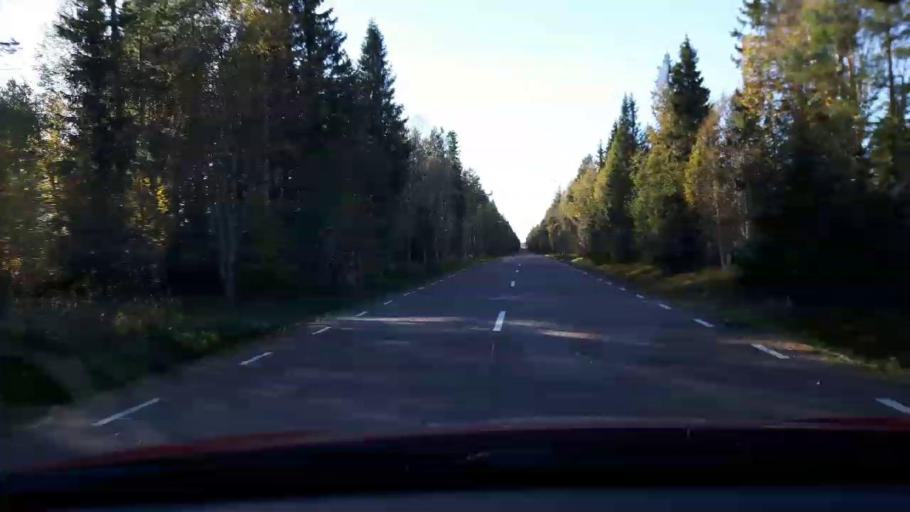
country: SE
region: Jaemtland
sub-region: Stroemsunds Kommun
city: Stroemsund
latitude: 63.8514
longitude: 15.2515
